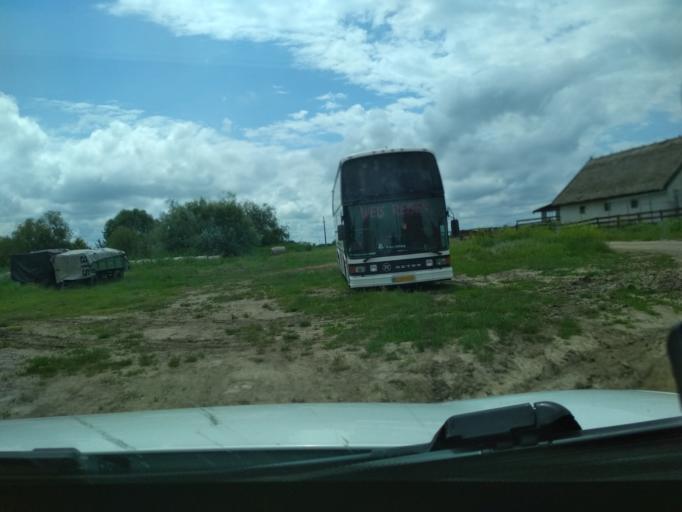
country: HU
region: Jasz-Nagykun-Szolnok
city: Tiszaszolos
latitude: 47.6001
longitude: 20.7207
